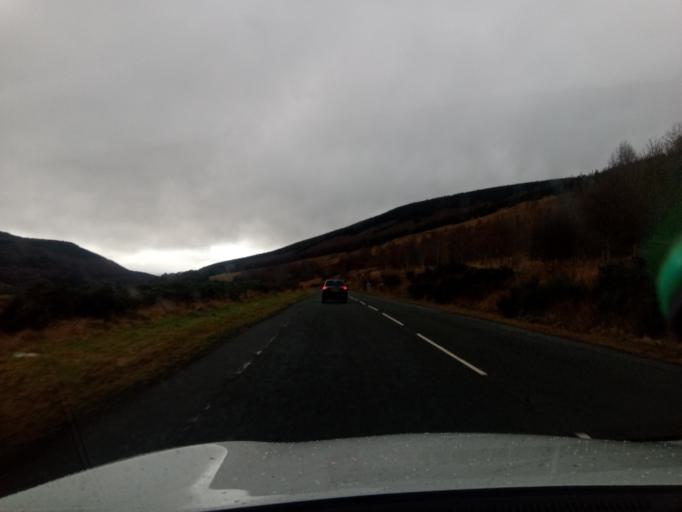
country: GB
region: Scotland
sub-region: The Scottish Borders
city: Innerleithen
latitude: 55.6297
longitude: -2.9916
